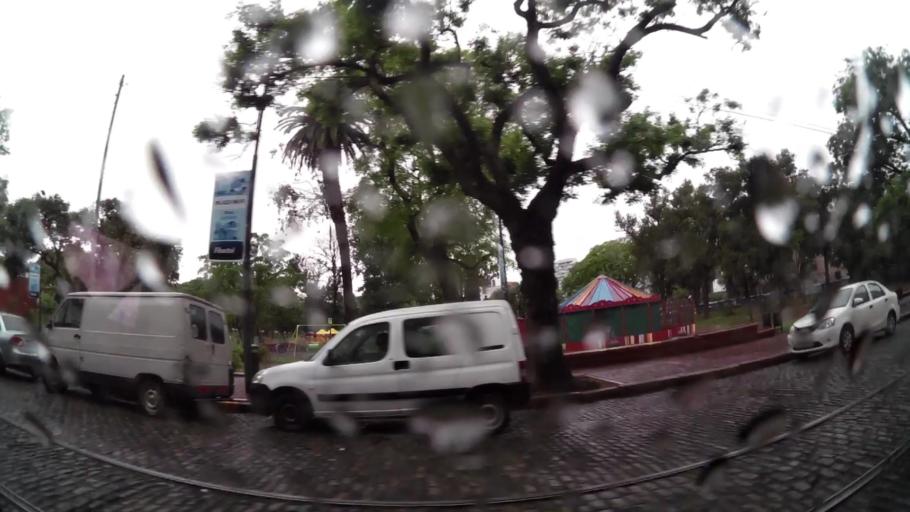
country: AR
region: Buenos Aires F.D.
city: Buenos Aires
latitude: -34.6280
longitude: -58.3709
